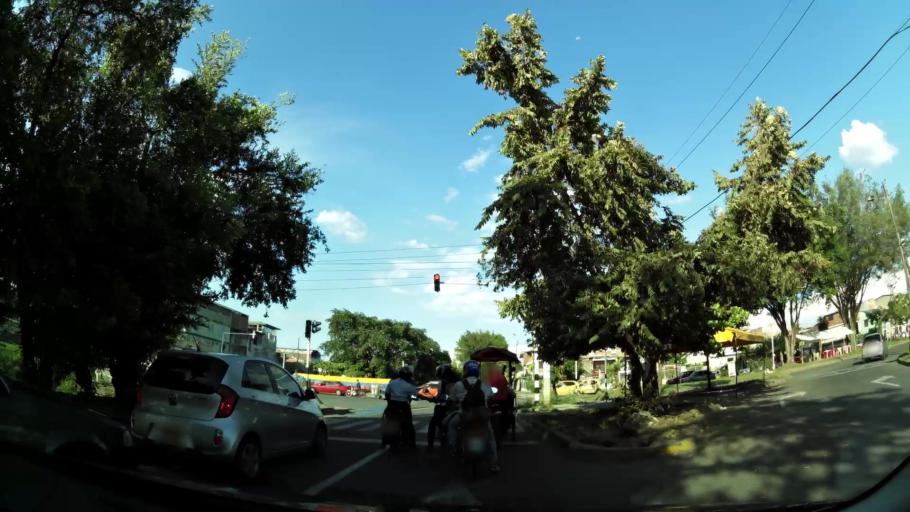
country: CO
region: Valle del Cauca
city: Cali
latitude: 3.4047
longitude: -76.5078
